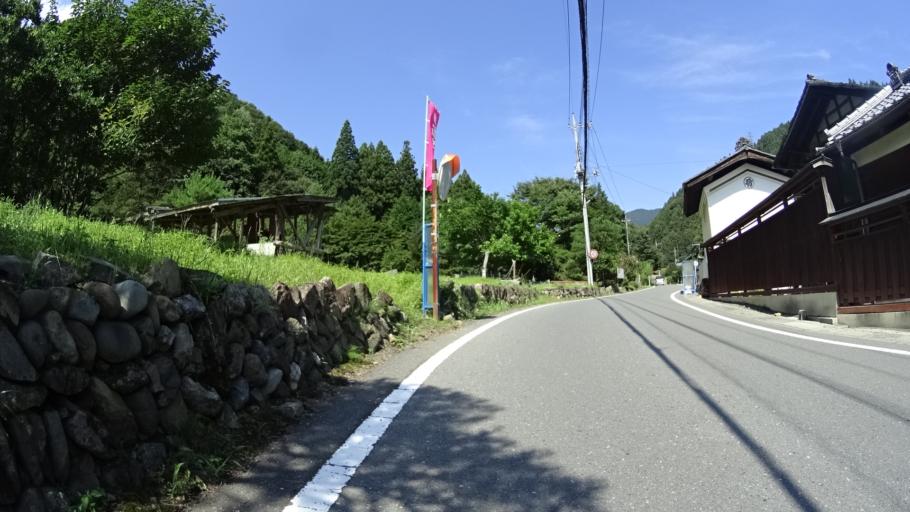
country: JP
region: Gunma
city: Tomioka
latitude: 36.0503
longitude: 138.8768
